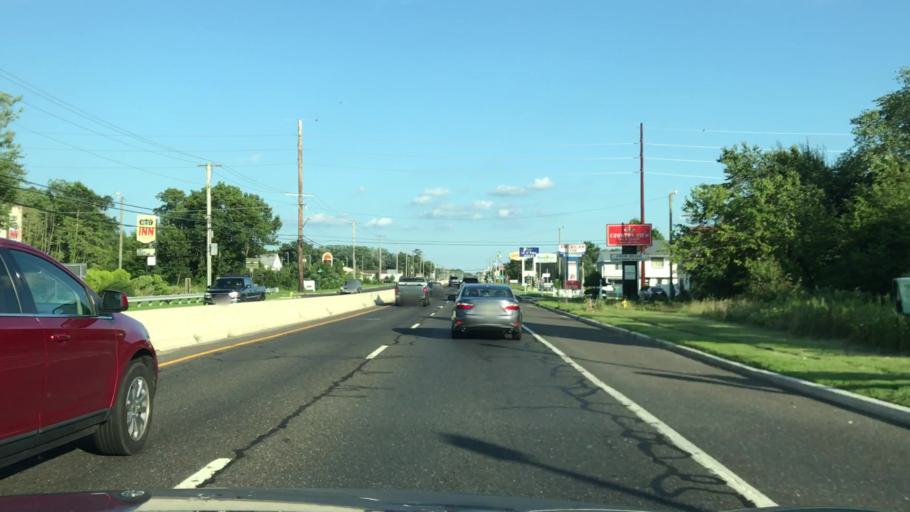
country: US
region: New Jersey
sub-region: Atlantic County
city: Absecon
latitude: 39.4481
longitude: -74.5315
